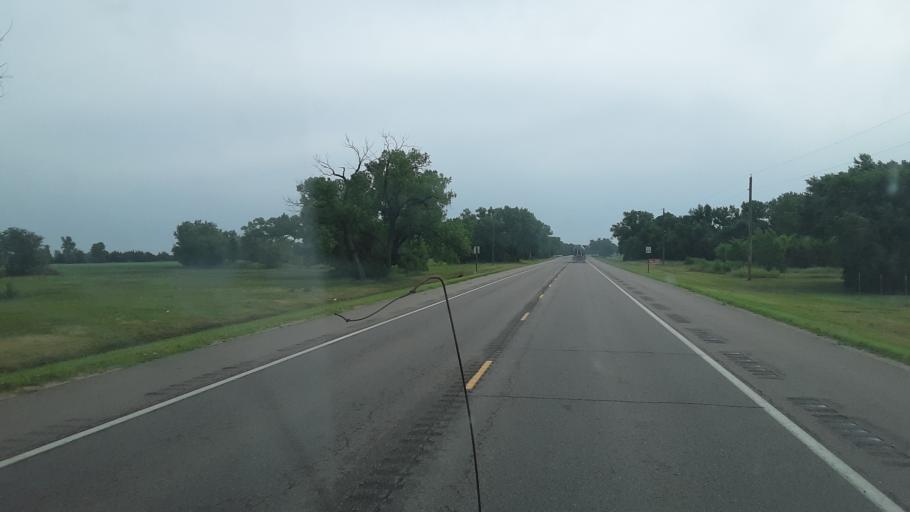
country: US
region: Kansas
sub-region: Edwards County
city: Kinsley
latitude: 37.9213
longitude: -99.3984
